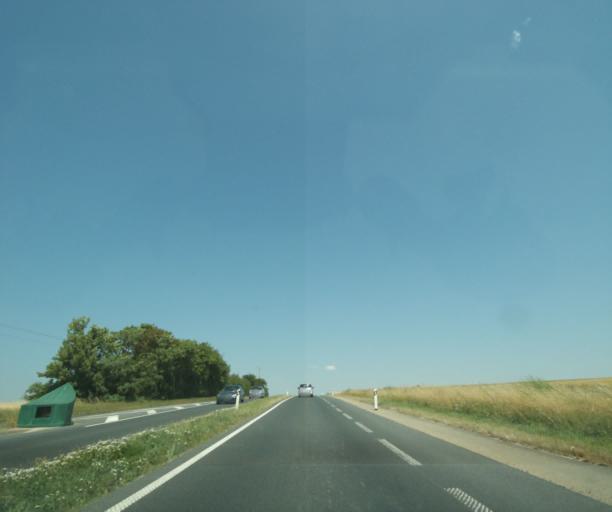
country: FR
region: Champagne-Ardenne
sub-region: Departement de la Marne
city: Mourmelon-le-Grand
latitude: 49.0752
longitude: 4.2872
